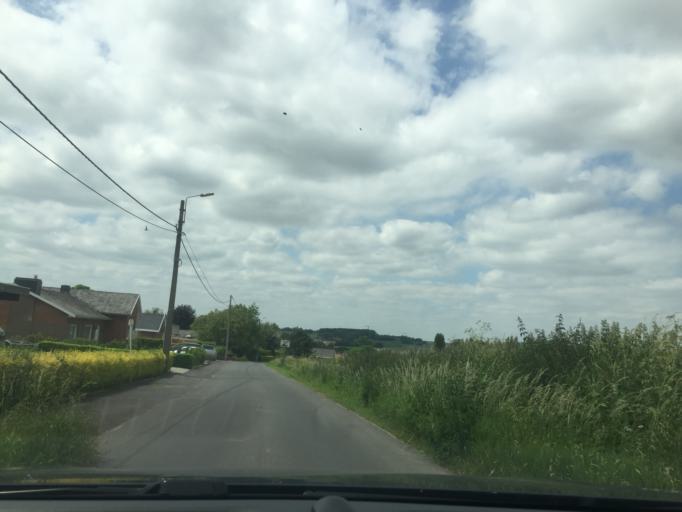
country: BE
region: Flanders
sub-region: Provincie West-Vlaanderen
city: Zwevegem
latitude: 50.7562
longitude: 3.3584
